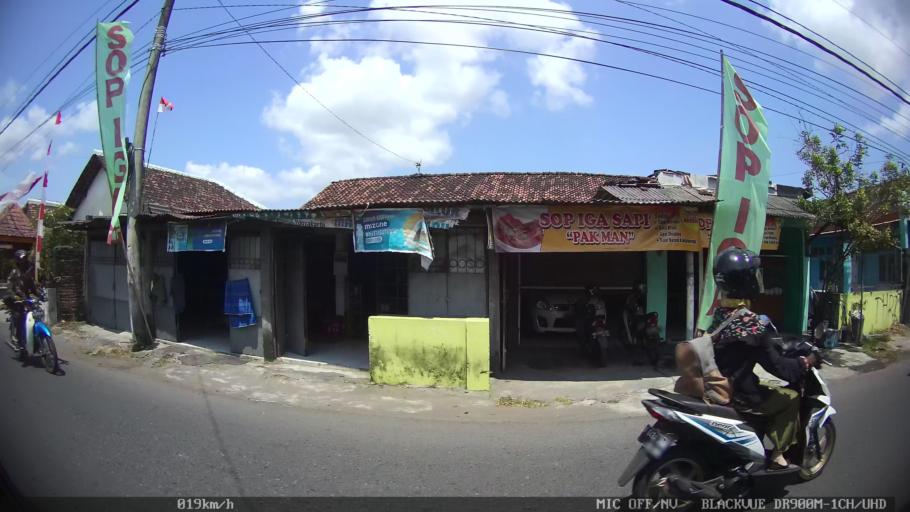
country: ID
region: Daerah Istimewa Yogyakarta
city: Sewon
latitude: -7.8947
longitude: 110.3496
